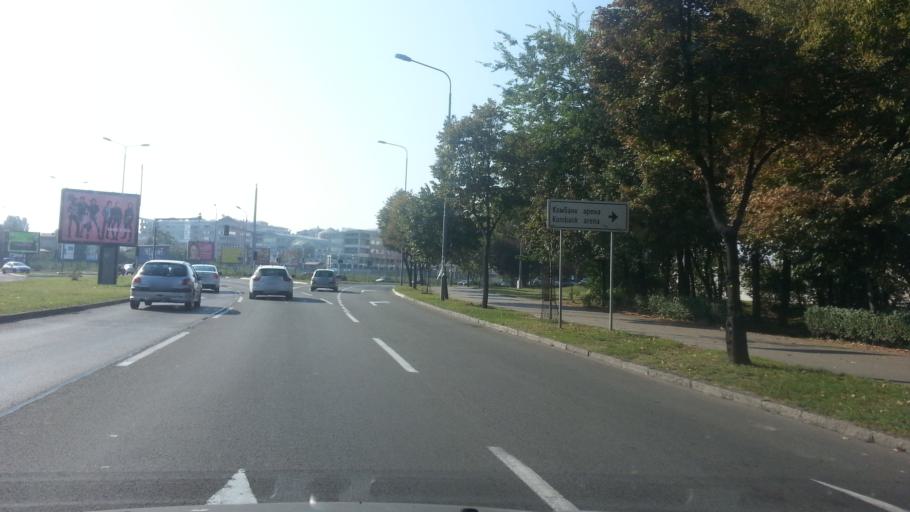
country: RS
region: Central Serbia
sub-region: Belgrade
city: Novi Beograd
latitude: 44.8264
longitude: 20.4199
